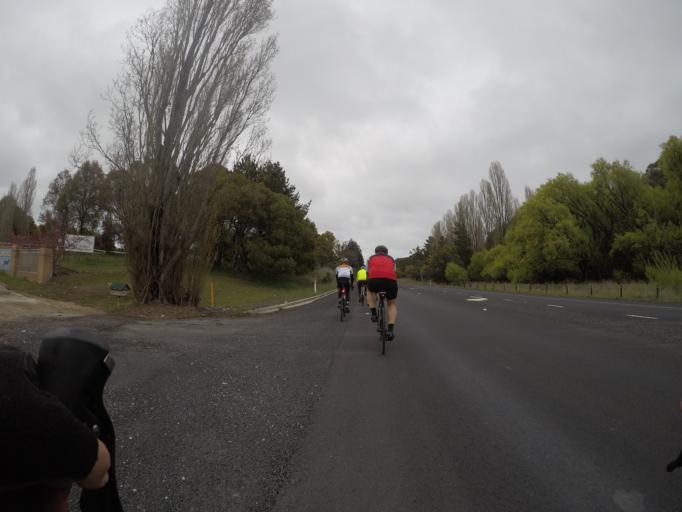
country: AU
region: New South Wales
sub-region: Lithgow
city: Portland
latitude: -33.4331
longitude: 149.8772
